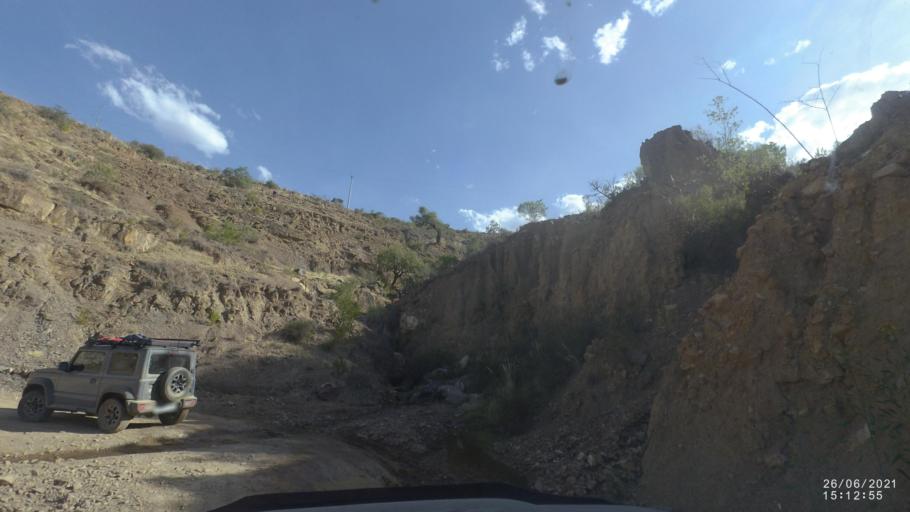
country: BO
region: Cochabamba
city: Mizque
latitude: -17.9594
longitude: -65.6442
